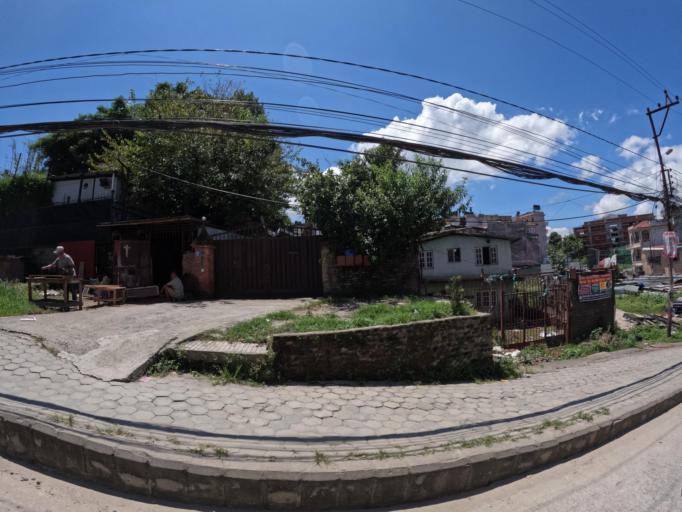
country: NP
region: Central Region
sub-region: Bagmati Zone
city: Kathmandu
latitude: 27.7455
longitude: 85.3280
